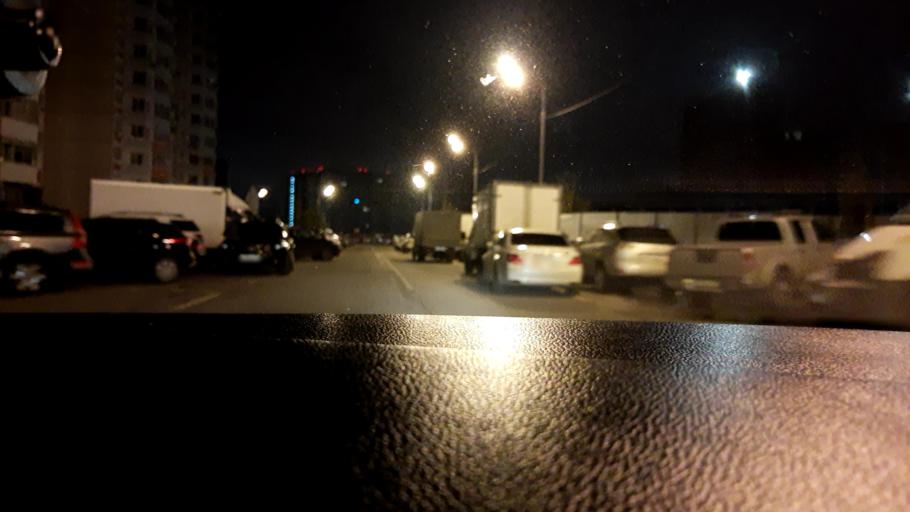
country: RU
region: Moscow
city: Khimki
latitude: 55.8724
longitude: 37.3911
